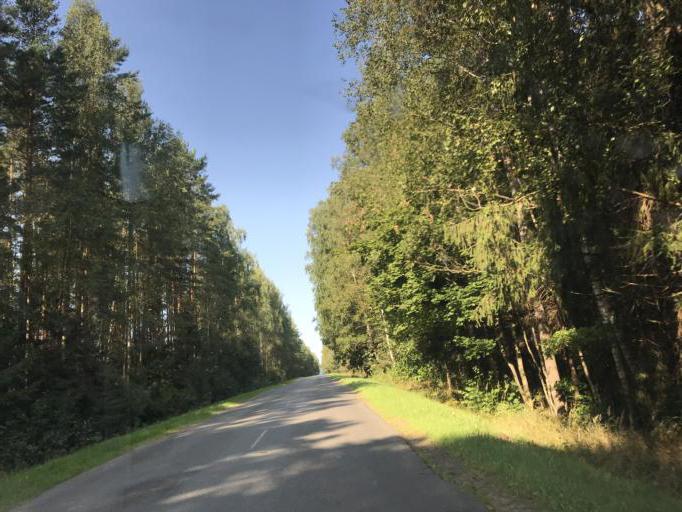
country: BY
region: Mogilev
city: Myazhysyatki
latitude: 53.8008
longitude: 30.1747
